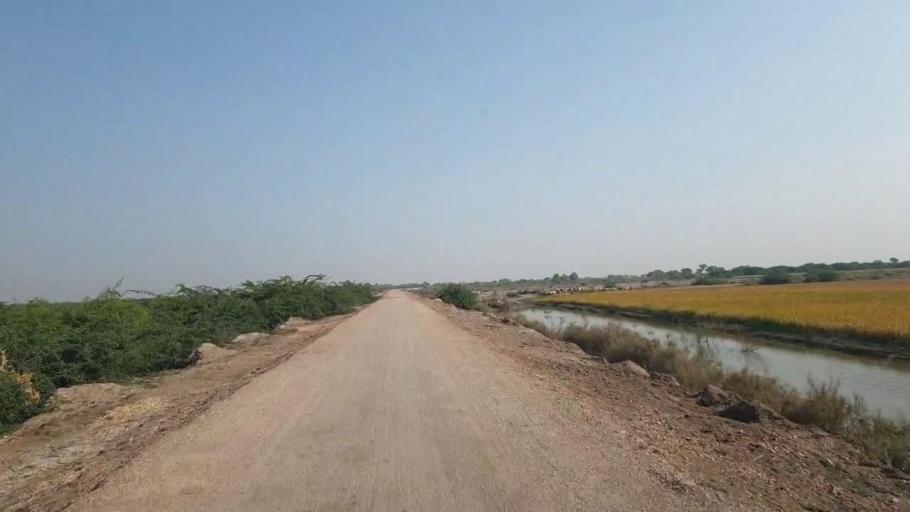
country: PK
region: Sindh
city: Badin
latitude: 24.4869
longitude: 68.7479
